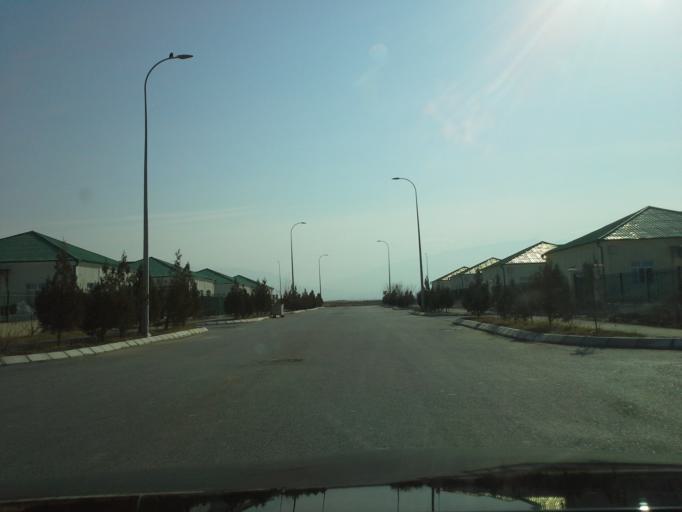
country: TM
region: Ahal
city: Abadan
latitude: 38.1657
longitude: 58.0502
